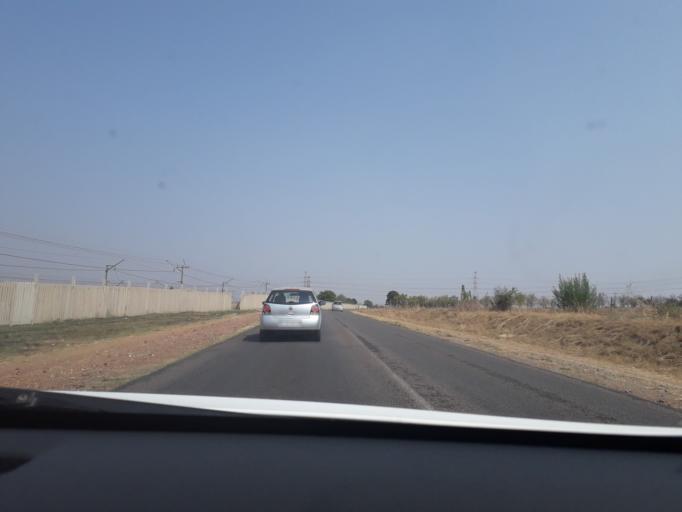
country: ZA
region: Gauteng
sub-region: City of Tshwane Metropolitan Municipality
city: Centurion
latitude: -25.8923
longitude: 28.2244
